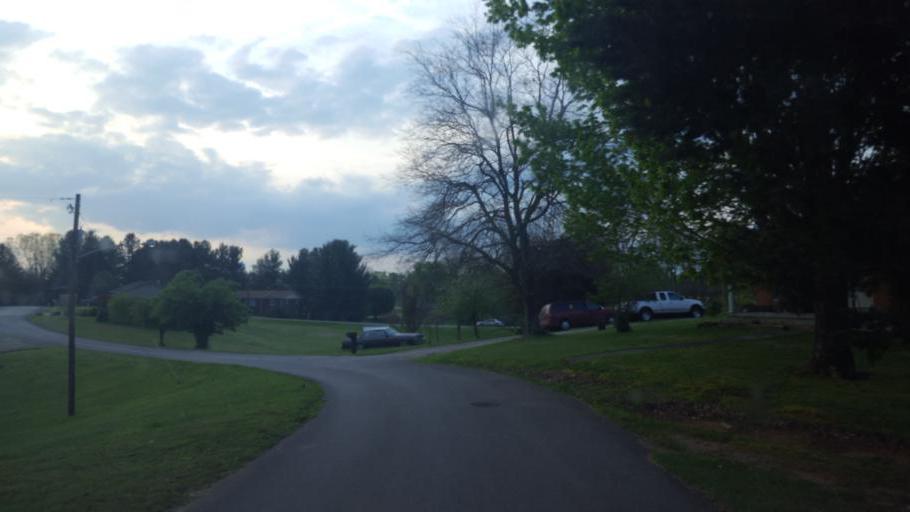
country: US
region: Kentucky
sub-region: Hart County
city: Munfordville
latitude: 37.2791
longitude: -85.9016
